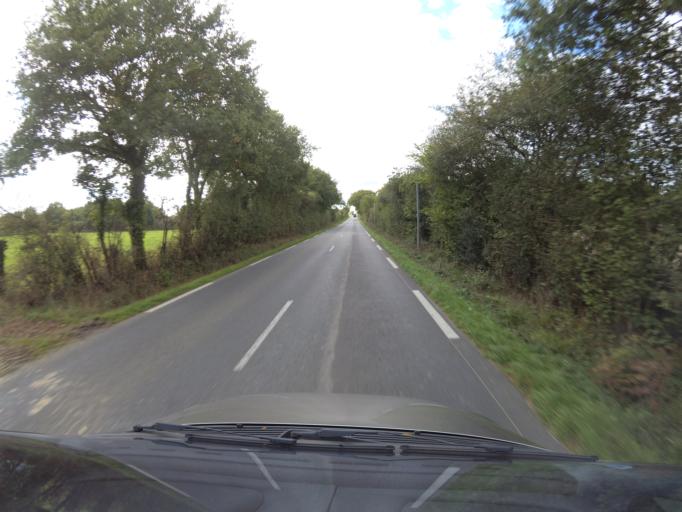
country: FR
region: Pays de la Loire
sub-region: Departement de la Loire-Atlantique
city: Notre-Dame-des-Landes
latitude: 47.4095
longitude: -1.7134
